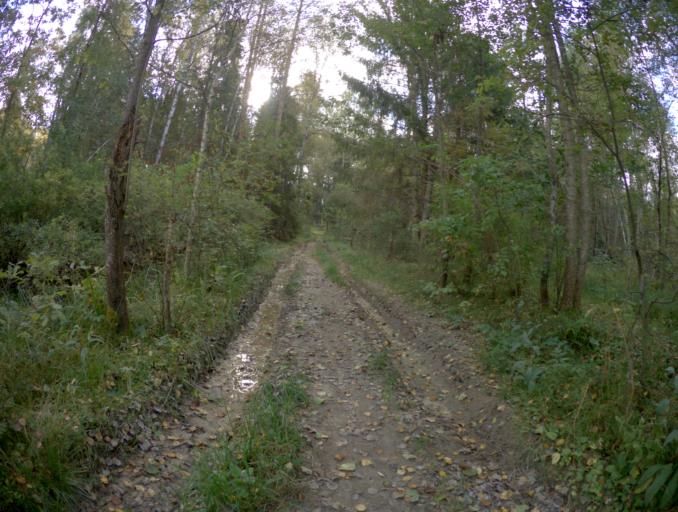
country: RU
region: Vladimir
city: Lakinsk
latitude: 55.9474
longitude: 39.7957
